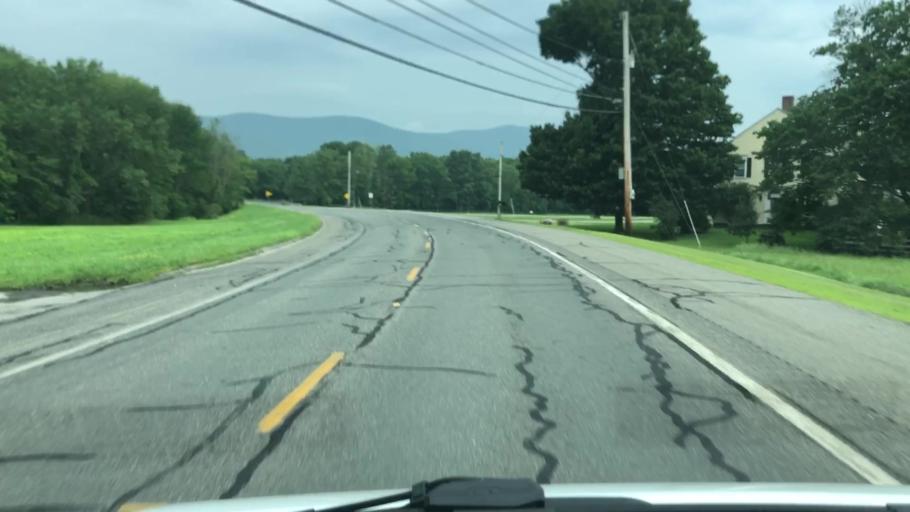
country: US
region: Massachusetts
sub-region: Berkshire County
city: Williamstown
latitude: 42.6421
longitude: -73.2306
